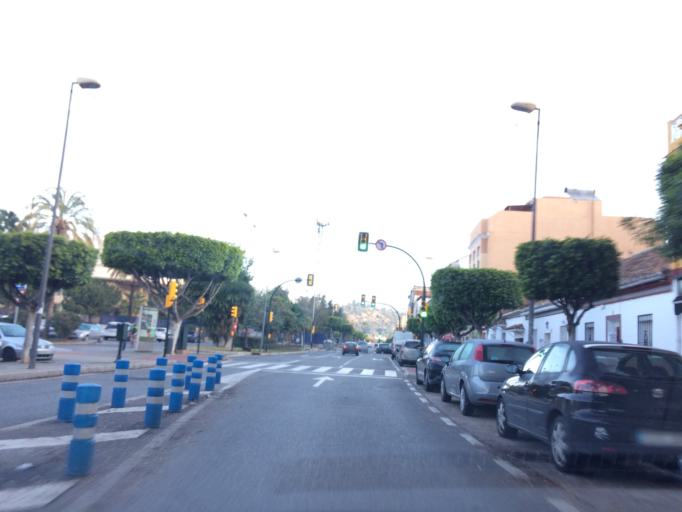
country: ES
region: Andalusia
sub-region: Provincia de Malaga
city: Malaga
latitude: 36.7498
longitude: -4.4222
